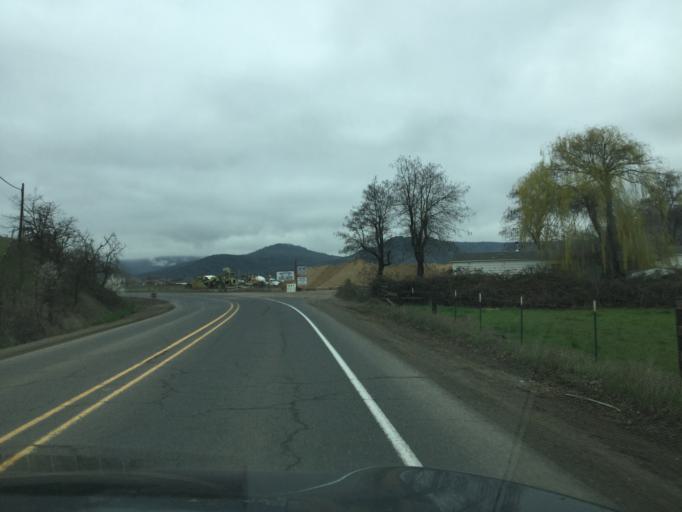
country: US
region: Oregon
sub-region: Jackson County
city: Central Point
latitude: 42.4186
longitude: -122.9531
